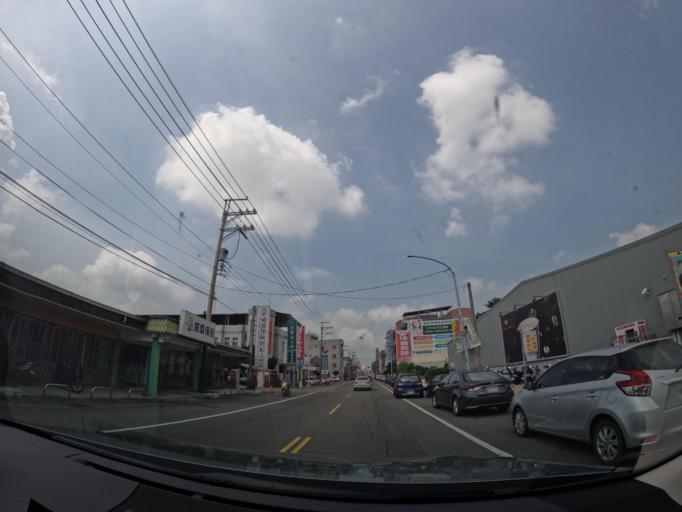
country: TW
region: Taiwan
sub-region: Yunlin
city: Douliu
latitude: 23.7095
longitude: 120.4449
